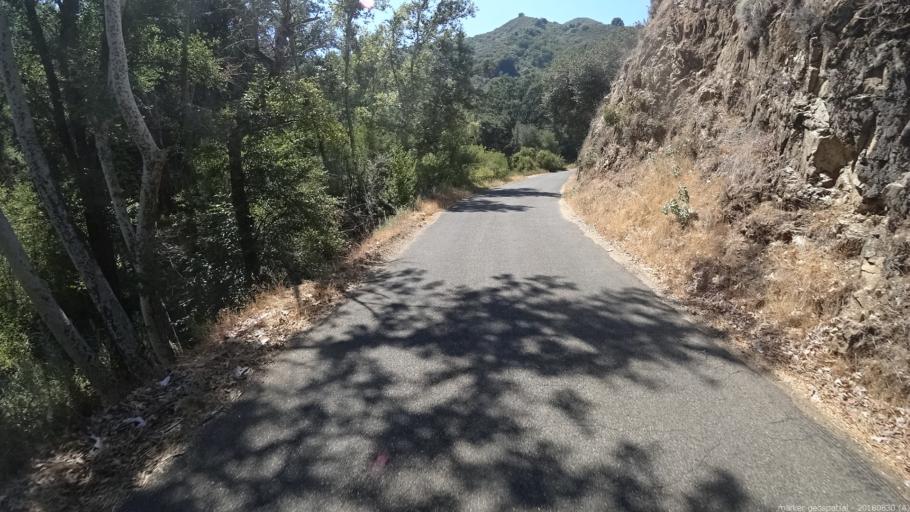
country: US
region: California
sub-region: Monterey County
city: King City
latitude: 36.0045
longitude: -121.3950
